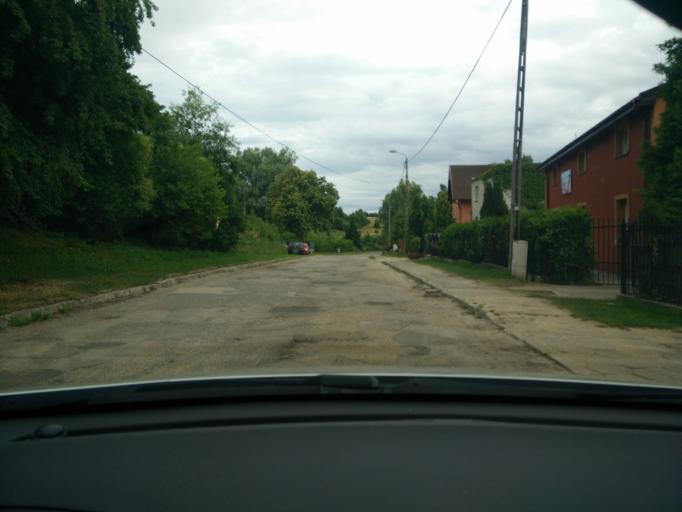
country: PL
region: Pomeranian Voivodeship
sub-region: Powiat pucki
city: Mrzezino
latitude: 54.6657
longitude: 18.4558
